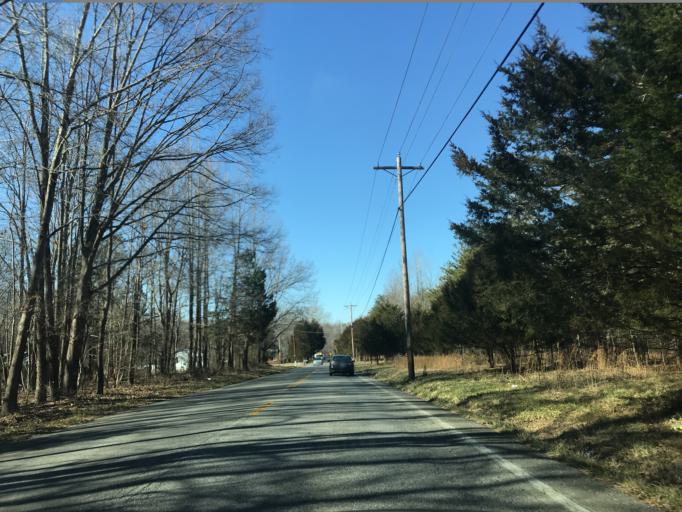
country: US
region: Maryland
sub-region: Charles County
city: Bennsville
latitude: 38.5889
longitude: -77.0490
